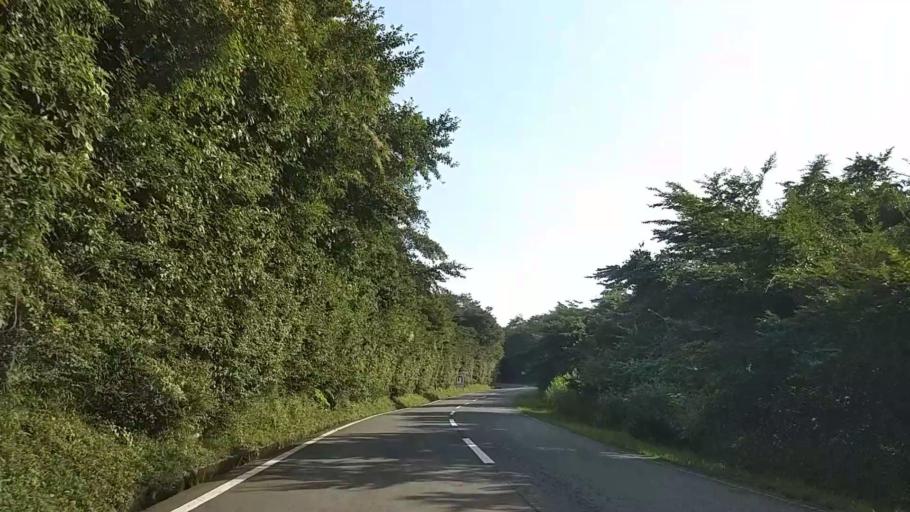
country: JP
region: Kanagawa
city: Hakone
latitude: 35.2297
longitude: 138.9787
